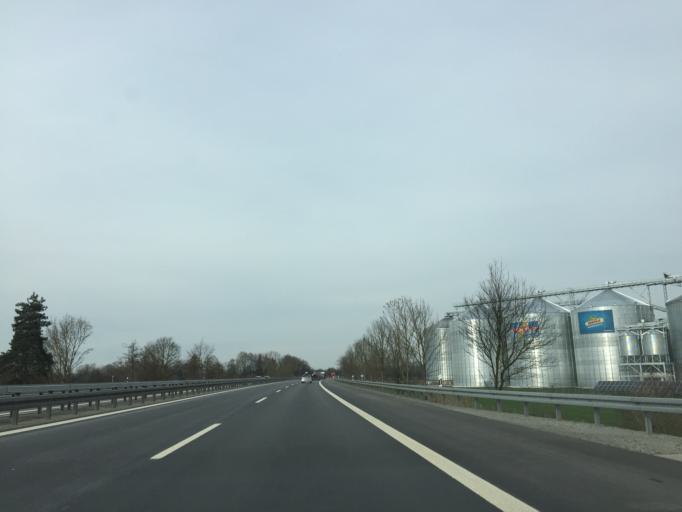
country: AT
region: Upper Austria
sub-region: Politischer Bezirk Scharding
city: Sankt Florian am Inn
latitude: 48.4215
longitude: 13.3948
